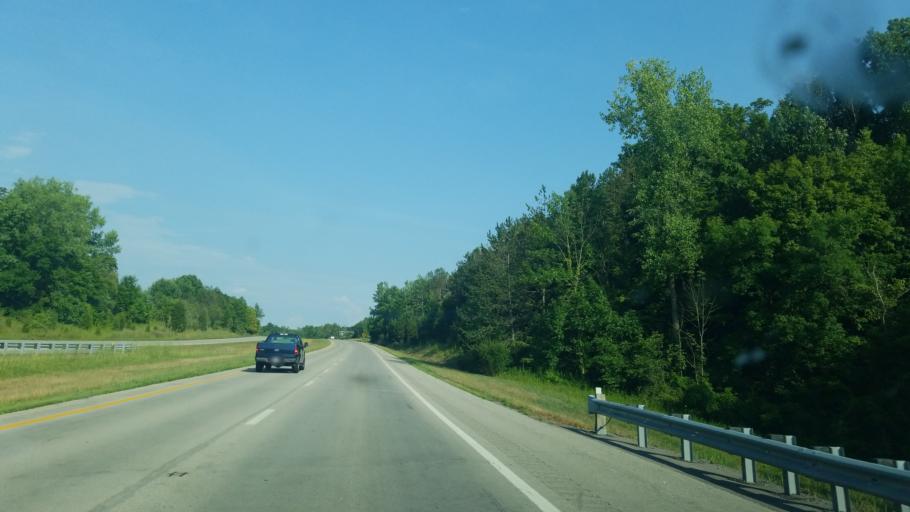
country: US
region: Ohio
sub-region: Brown County
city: Mount Orab
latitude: 39.0225
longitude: -83.8698
